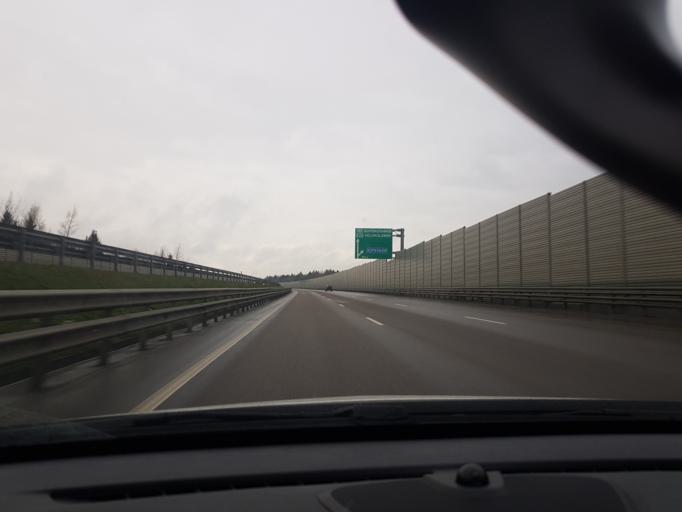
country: RU
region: Moskovskaya
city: Novopetrovskoye
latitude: 55.9749
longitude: 36.4808
